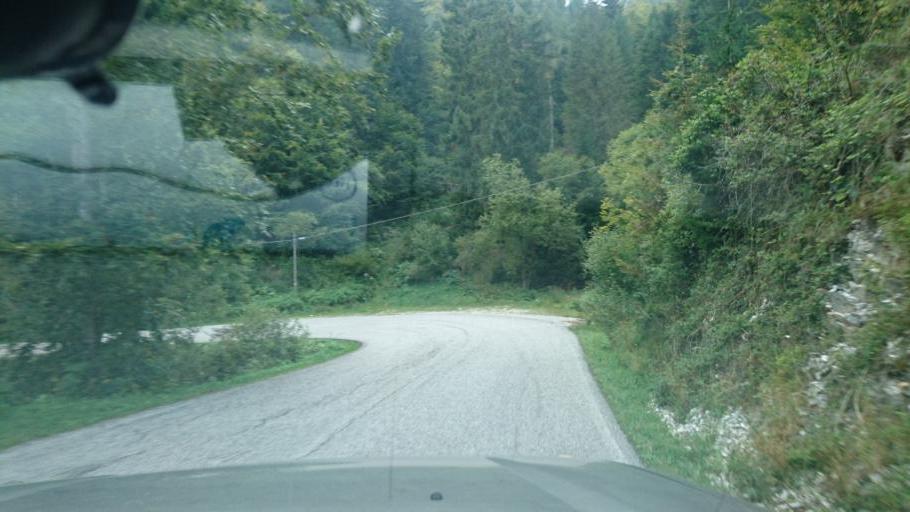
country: IT
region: Veneto
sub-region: Provincia di Vicenza
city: Enego
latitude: 45.9404
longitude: 11.6769
